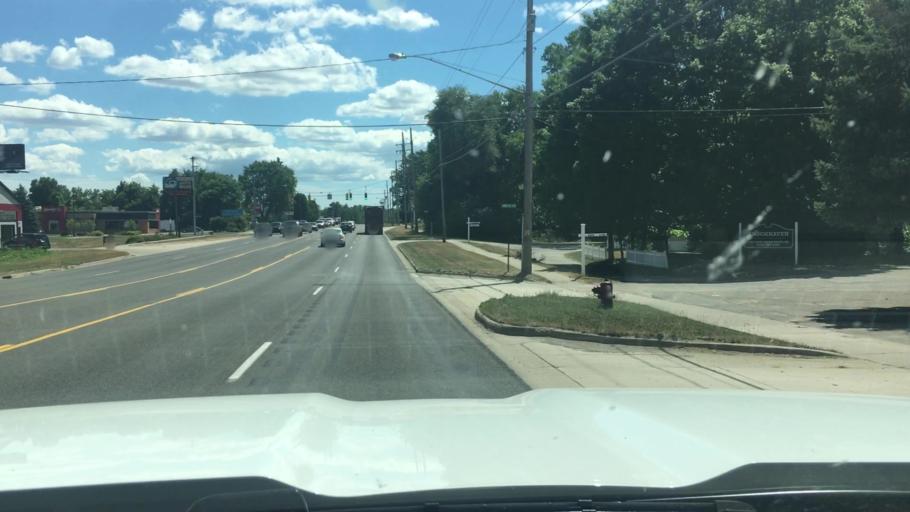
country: US
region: Michigan
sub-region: Kent County
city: Comstock Park
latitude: 43.0496
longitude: -85.6542
